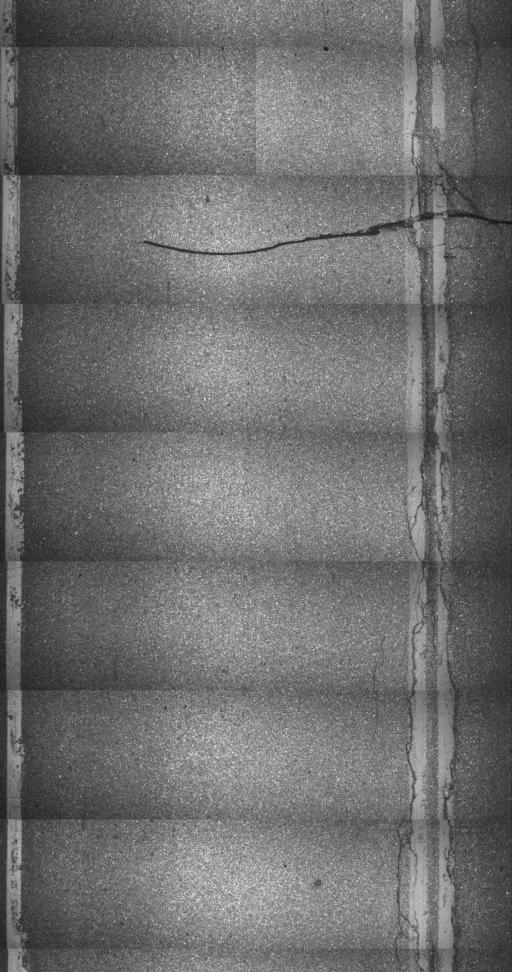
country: US
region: Vermont
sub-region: Orange County
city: Randolph
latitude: 43.9121
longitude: -72.8322
